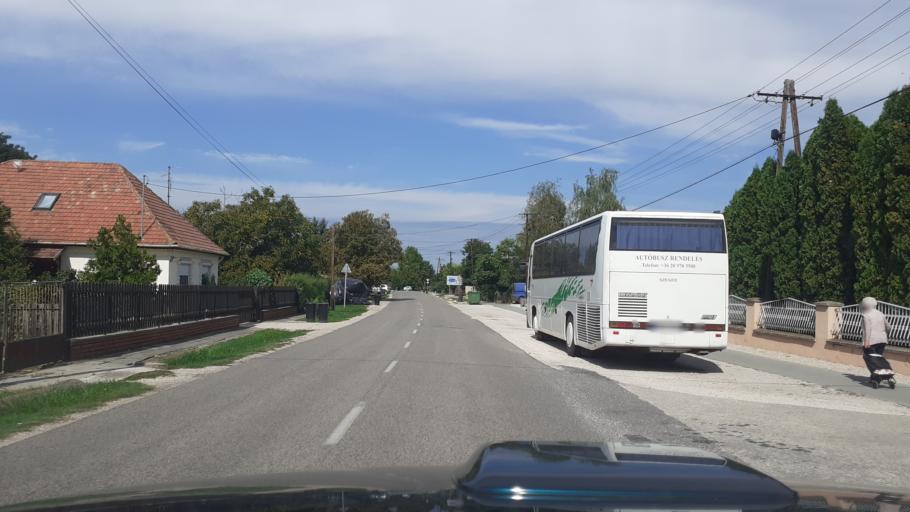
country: HU
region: Fejer
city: Pakozd
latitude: 47.1762
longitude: 18.5641
